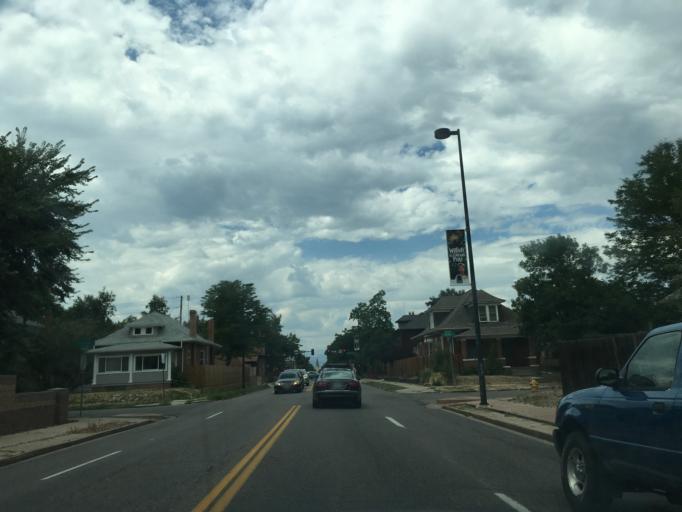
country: US
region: Colorado
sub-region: Denver County
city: Denver
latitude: 39.7111
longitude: -104.9751
